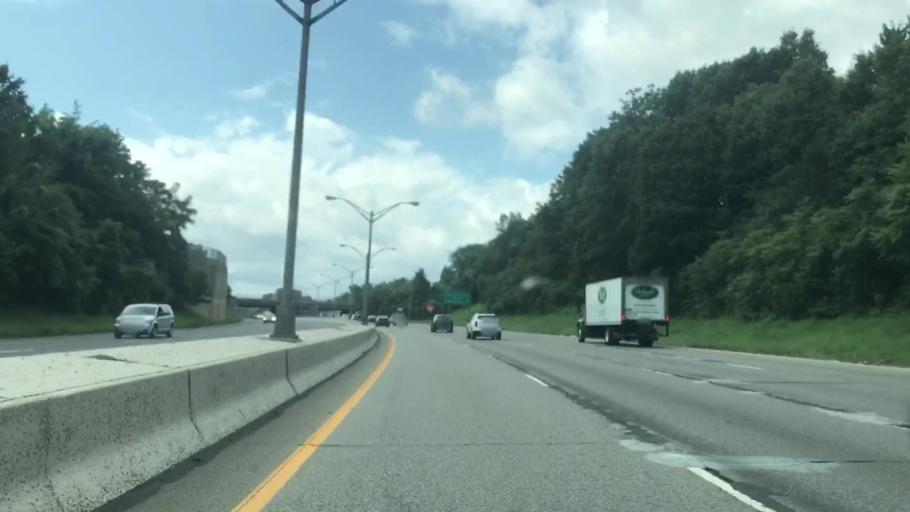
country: US
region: New Jersey
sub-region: Middlesex County
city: Fords
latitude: 40.5272
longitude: -74.2869
